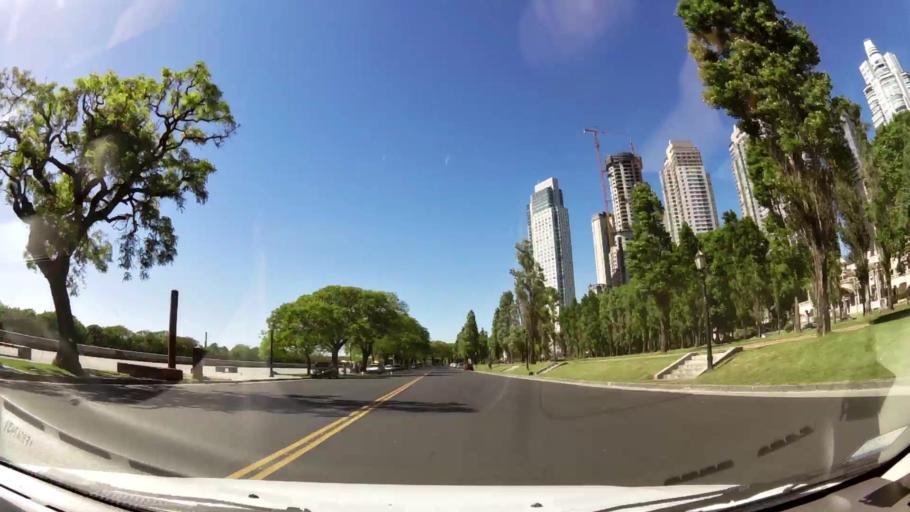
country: AR
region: Buenos Aires F.D.
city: Buenos Aires
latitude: -34.6087
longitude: -58.3594
